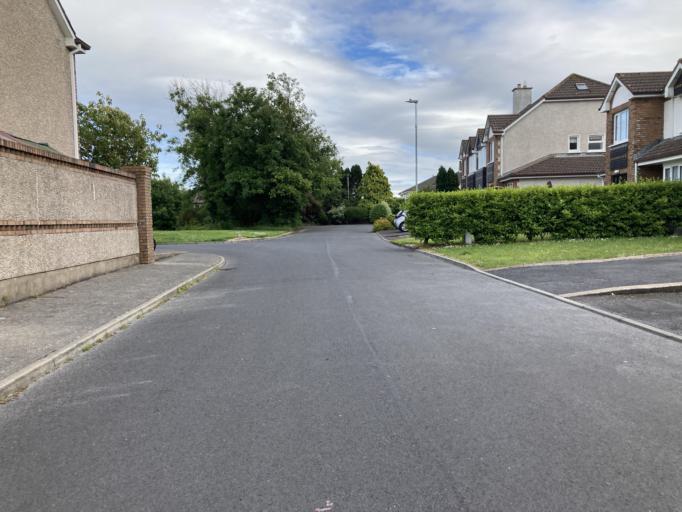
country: IE
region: Connaught
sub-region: County Galway
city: Bearna
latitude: 53.2630
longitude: -9.1209
